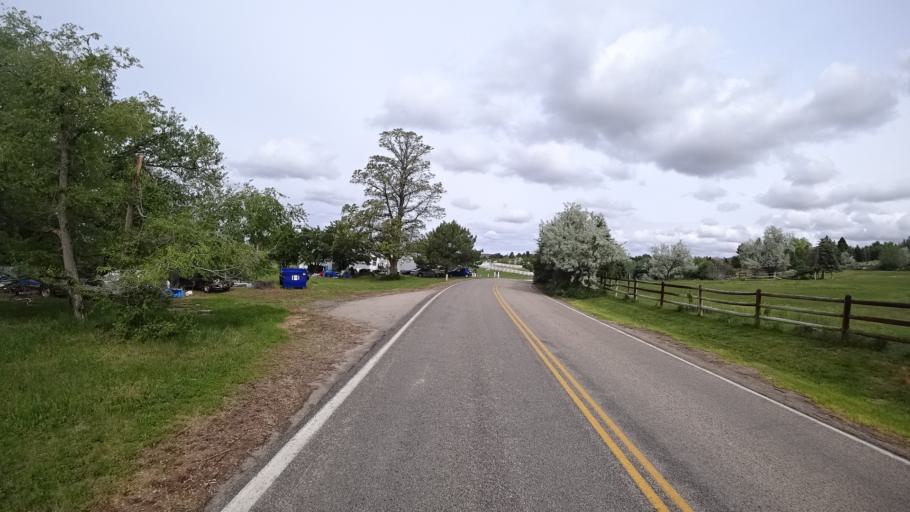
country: US
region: Idaho
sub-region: Ada County
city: Eagle
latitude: 43.7321
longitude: -116.3550
